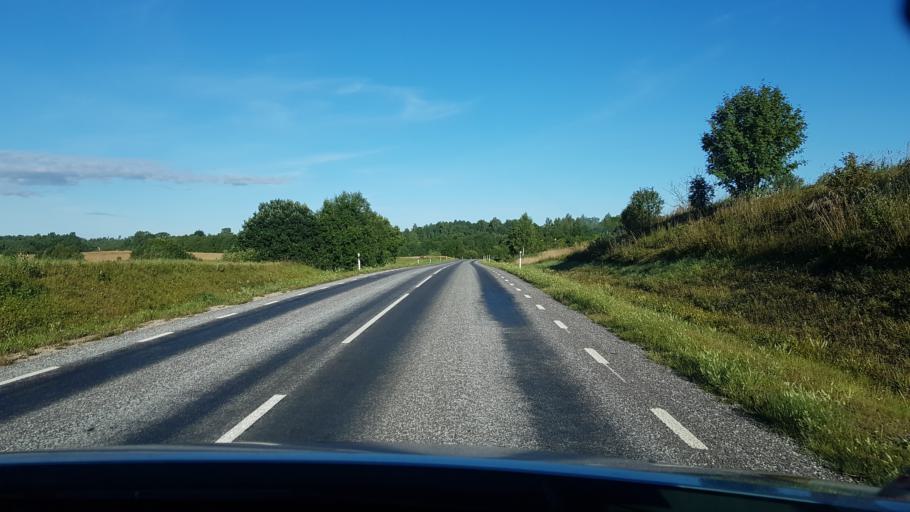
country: EE
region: Vorumaa
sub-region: Antsla vald
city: Vana-Antsla
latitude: 58.0073
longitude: 26.6060
